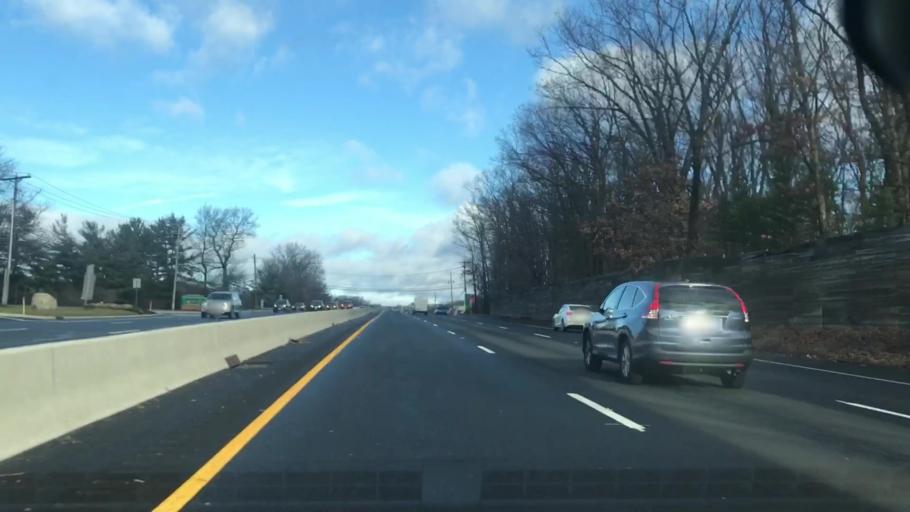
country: US
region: New Jersey
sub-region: Bergen County
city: Allendale
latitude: 41.0410
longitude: -74.1142
